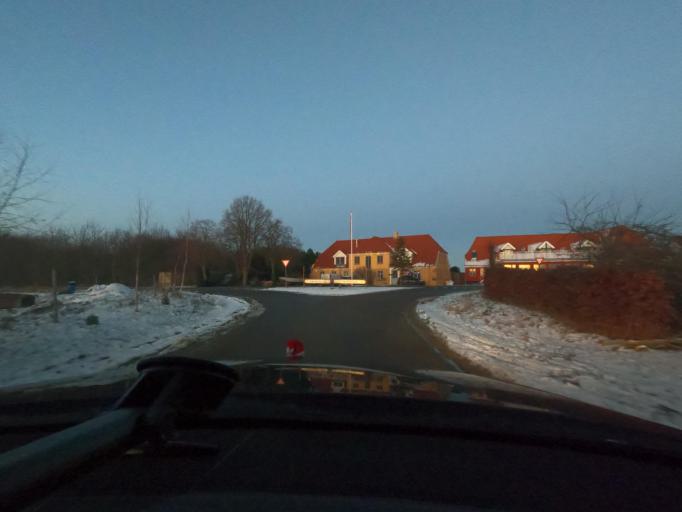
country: DK
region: South Denmark
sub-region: Sonderborg Kommune
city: Horuphav
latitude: 54.8684
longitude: 9.9509
